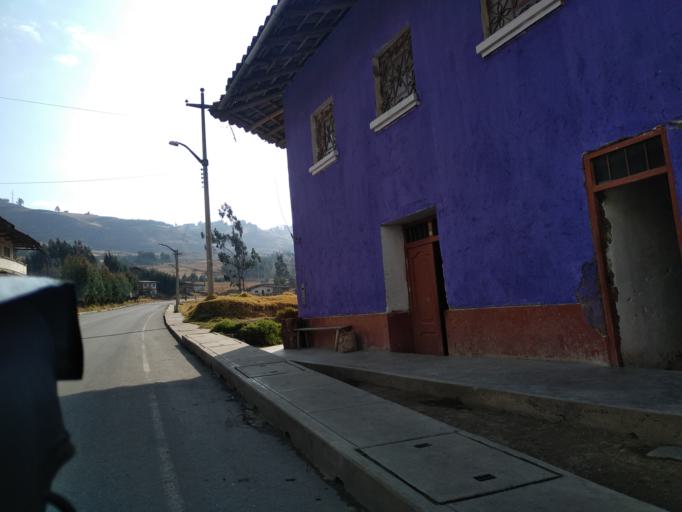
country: PE
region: La Libertad
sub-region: Provincia de Otuzco
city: Agallpampa
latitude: -7.9951
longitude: -78.5226
